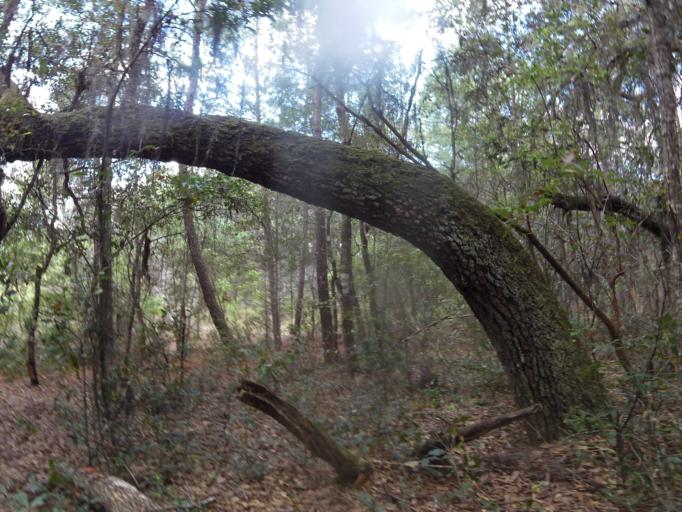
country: US
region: Florida
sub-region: Clay County
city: Keystone Heights
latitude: 29.7853
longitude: -81.8758
